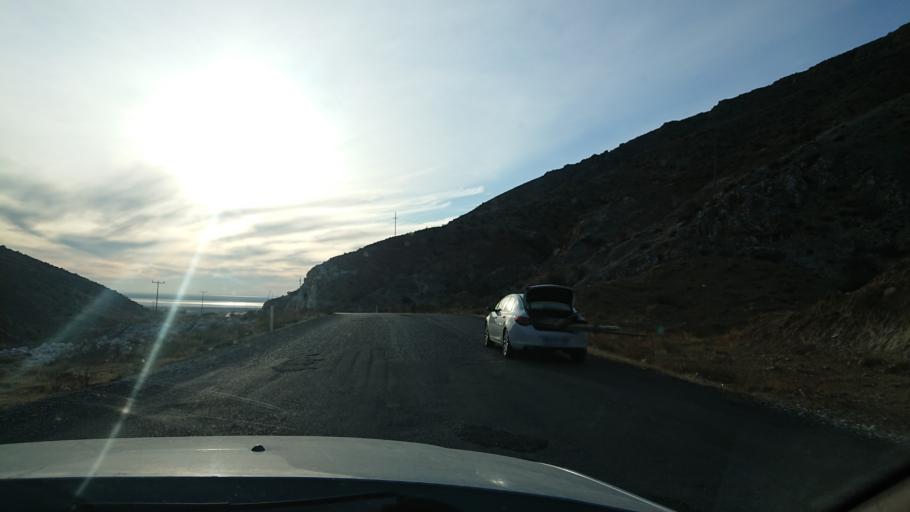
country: TR
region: Ankara
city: Sereflikochisar
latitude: 38.7495
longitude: 33.6883
